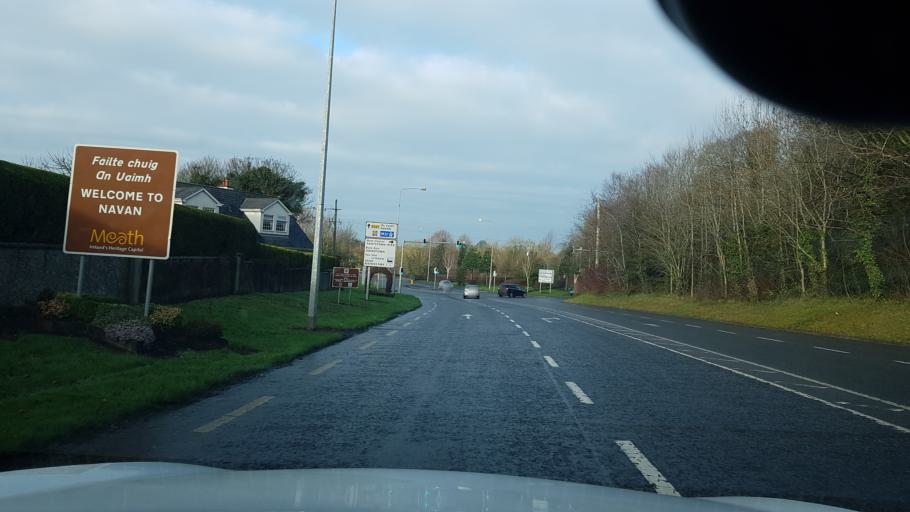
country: IE
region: Leinster
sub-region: An Mhi
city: Navan
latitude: 53.6302
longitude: -6.6590
